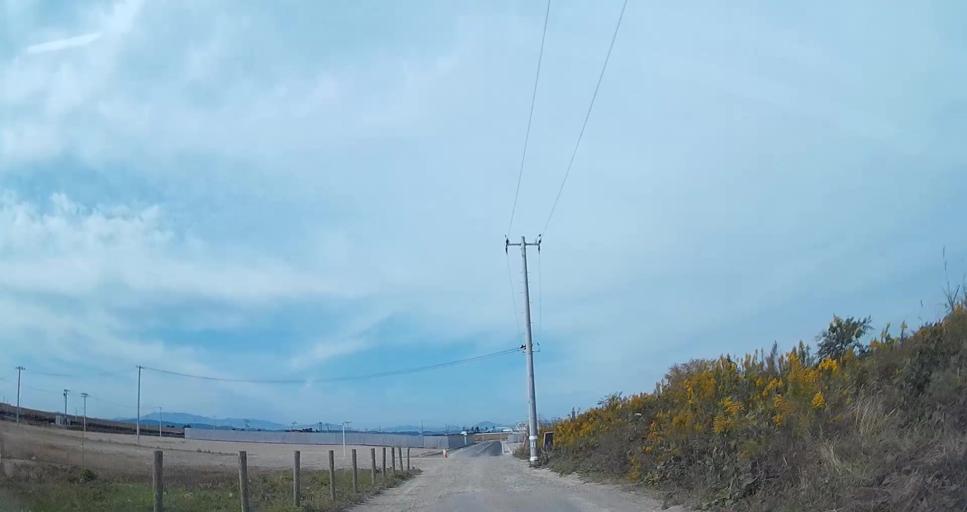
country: JP
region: Miyagi
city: Sendai
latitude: 38.1842
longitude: 140.9563
